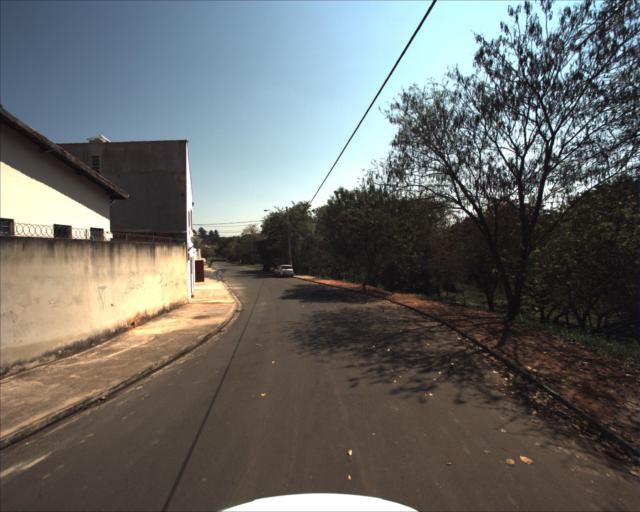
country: BR
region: Sao Paulo
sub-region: Sorocaba
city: Sorocaba
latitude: -23.4584
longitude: -47.4917
